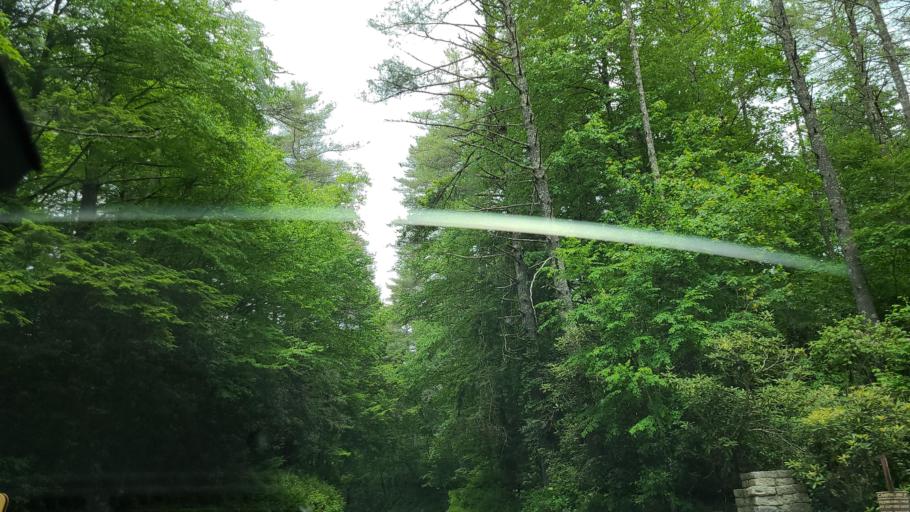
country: US
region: North Carolina
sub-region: Macon County
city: Franklin
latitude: 35.0764
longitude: -83.2467
